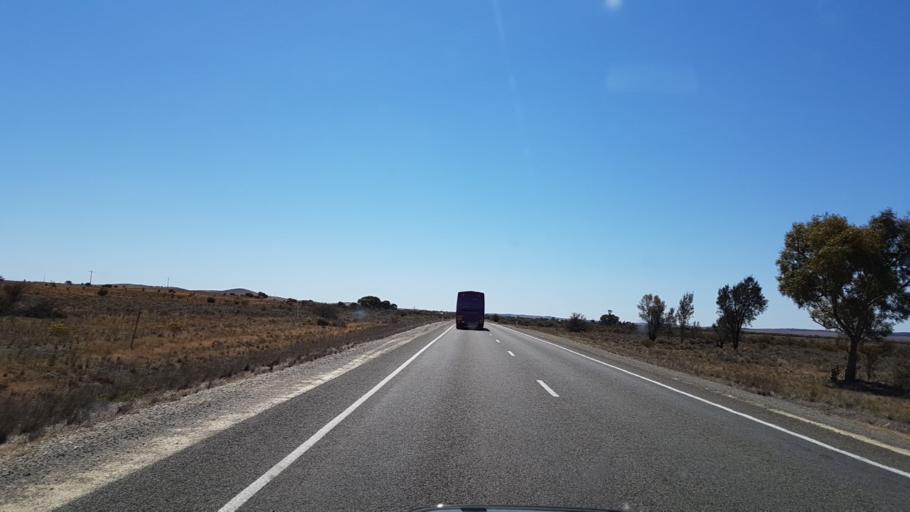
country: AU
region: South Australia
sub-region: Peterborough
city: Peterborough
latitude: -33.1767
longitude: 138.9083
